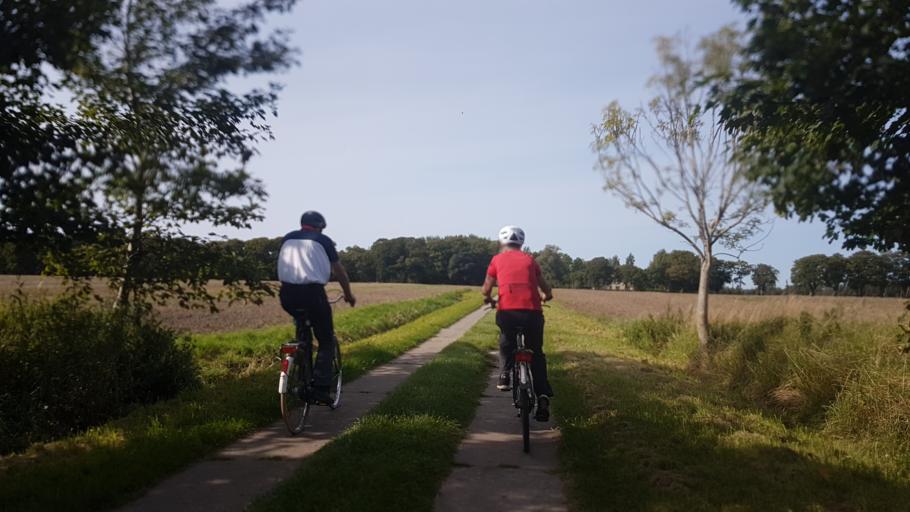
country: DE
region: Mecklenburg-Vorpommern
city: Gingst
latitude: 54.4398
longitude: 13.1888
